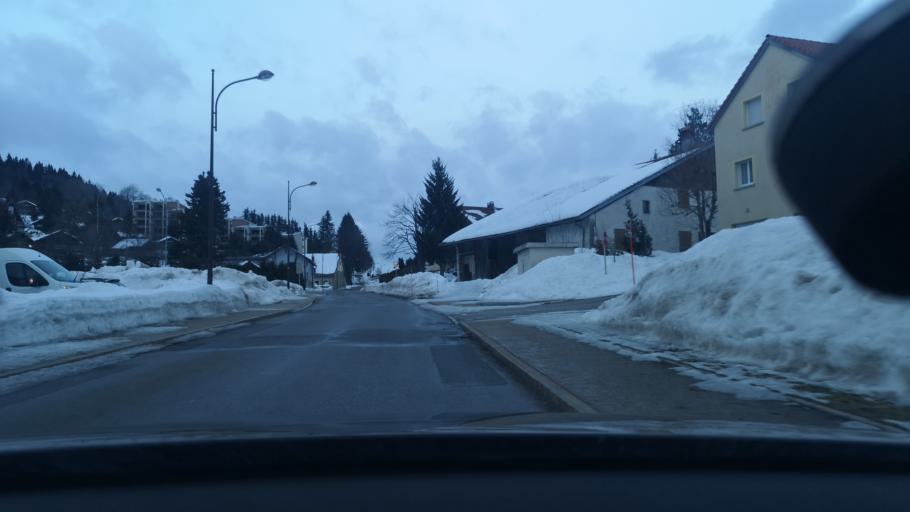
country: FR
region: Franche-Comte
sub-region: Departement du Doubs
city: Jougne
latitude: 46.7780
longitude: 6.3727
